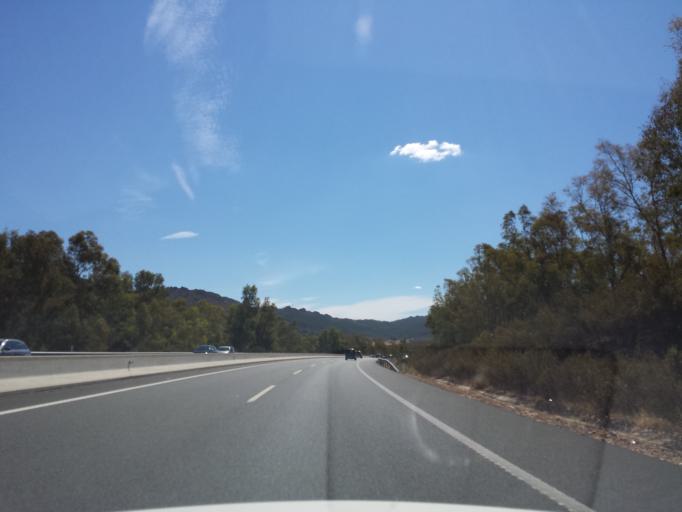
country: ES
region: Extremadura
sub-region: Provincia de Caceres
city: Romangordo
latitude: 39.7143
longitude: -5.7006
